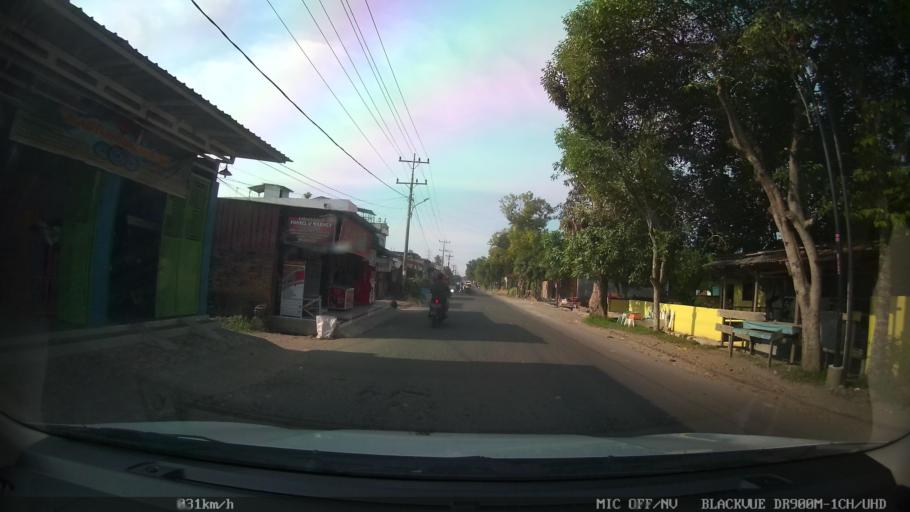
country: ID
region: North Sumatra
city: Binjai
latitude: 3.6176
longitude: 98.5183
